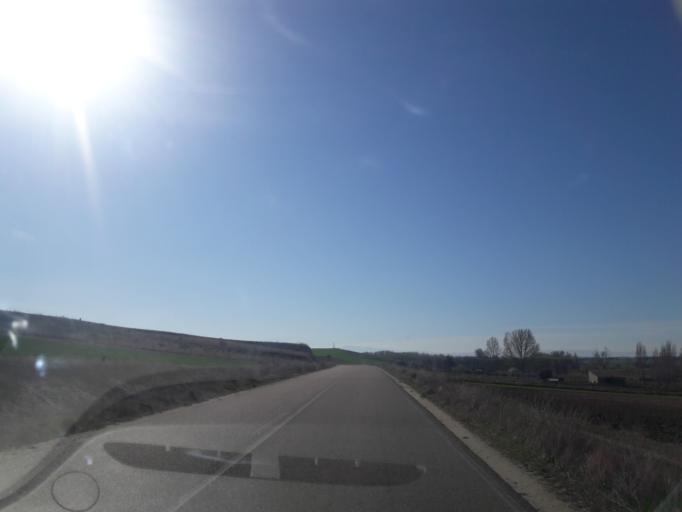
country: ES
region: Castille and Leon
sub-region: Provincia de Salamanca
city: Tordillos
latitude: 40.8561
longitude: -5.3479
